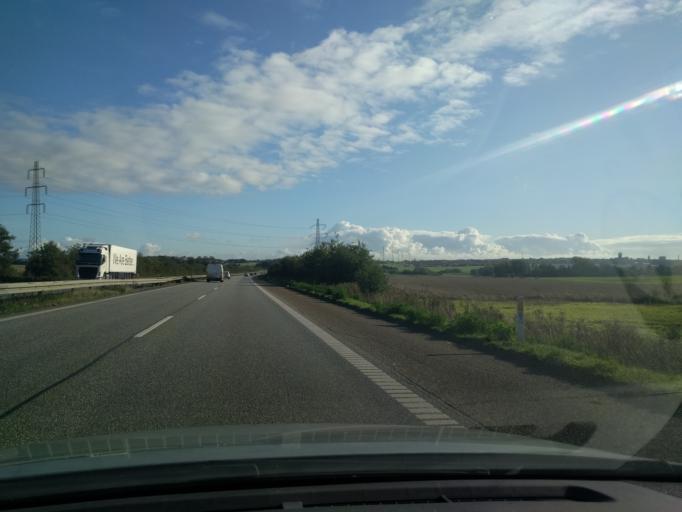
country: DK
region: Zealand
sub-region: Ringsted Kommune
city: Ringsted
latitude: 55.4548
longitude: 11.7435
